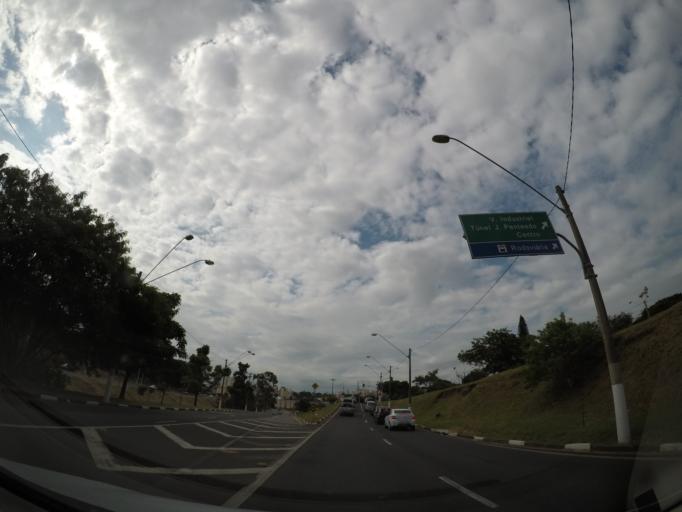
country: BR
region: Sao Paulo
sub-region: Campinas
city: Campinas
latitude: -22.9162
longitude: -47.0723
